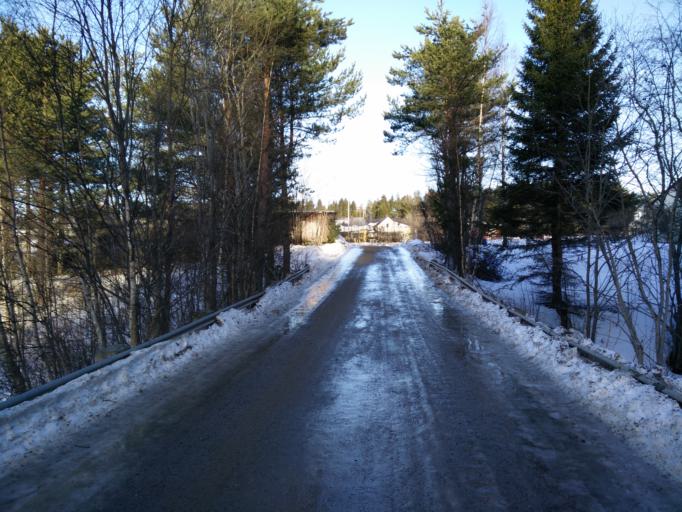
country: SE
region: Vaesternorrland
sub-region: Sundsvalls Kommun
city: Nolby
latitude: 62.2682
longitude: 17.3496
